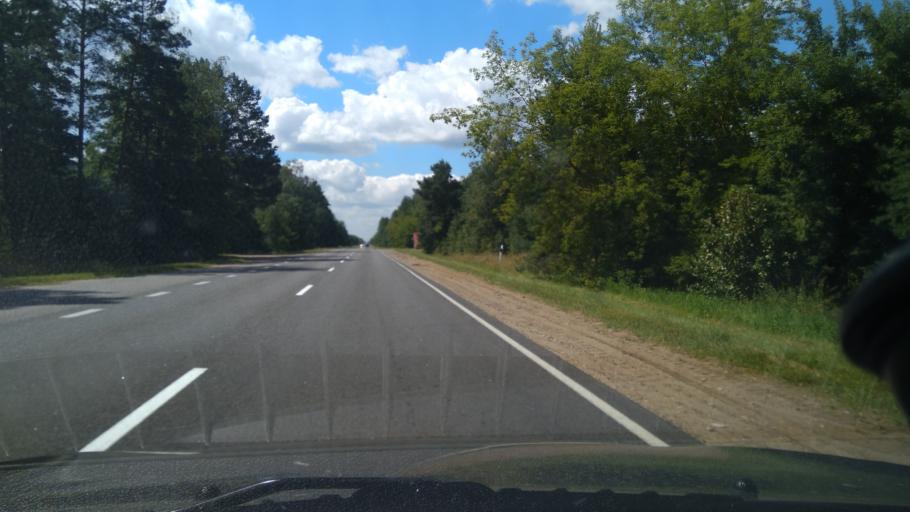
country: BY
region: Brest
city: Nyakhachava
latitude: 52.6583
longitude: 25.2345
